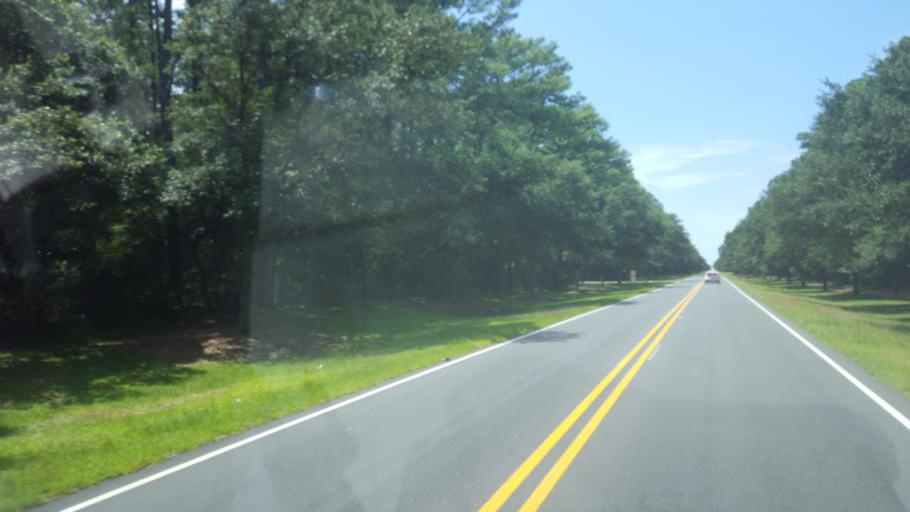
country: US
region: North Carolina
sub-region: Dare County
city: Manteo
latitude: 35.9321
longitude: -75.7095
